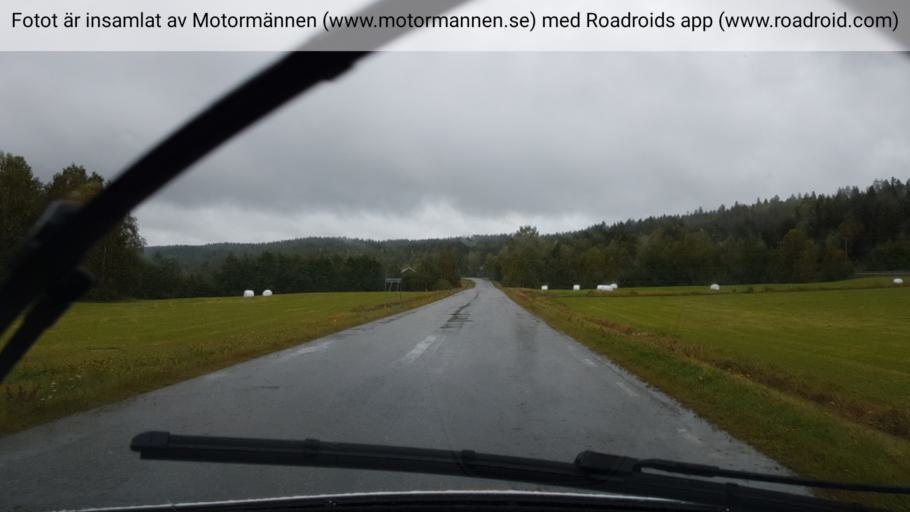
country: SE
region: Vaesterbotten
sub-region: Vannas Kommun
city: Vannasby
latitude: 64.1128
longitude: 19.9674
